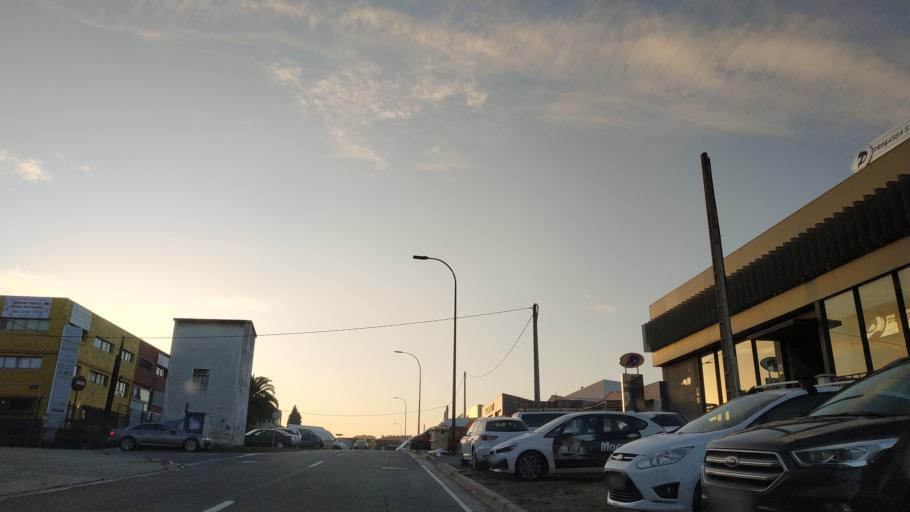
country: ES
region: Galicia
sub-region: Provincia da Coruna
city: A Coruna
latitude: 43.3561
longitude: -8.4190
